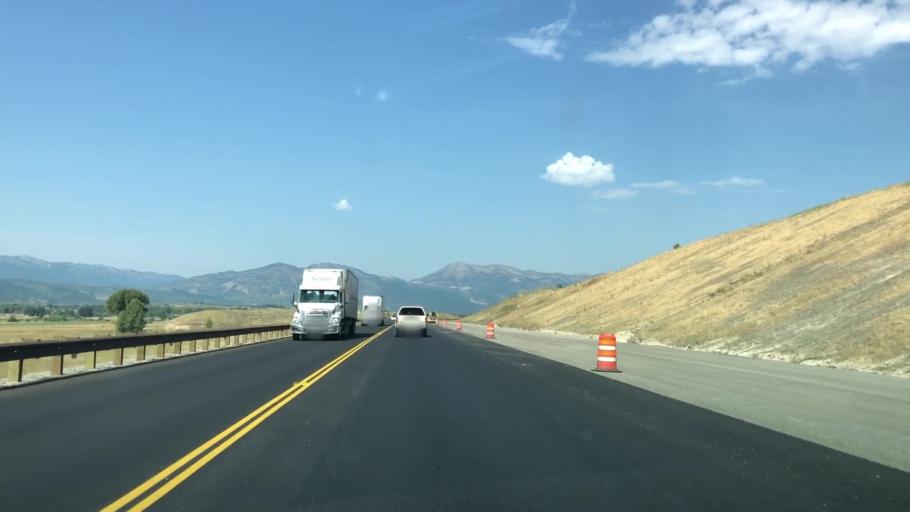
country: US
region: Wyoming
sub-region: Teton County
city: South Park
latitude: 43.4080
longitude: -110.7639
